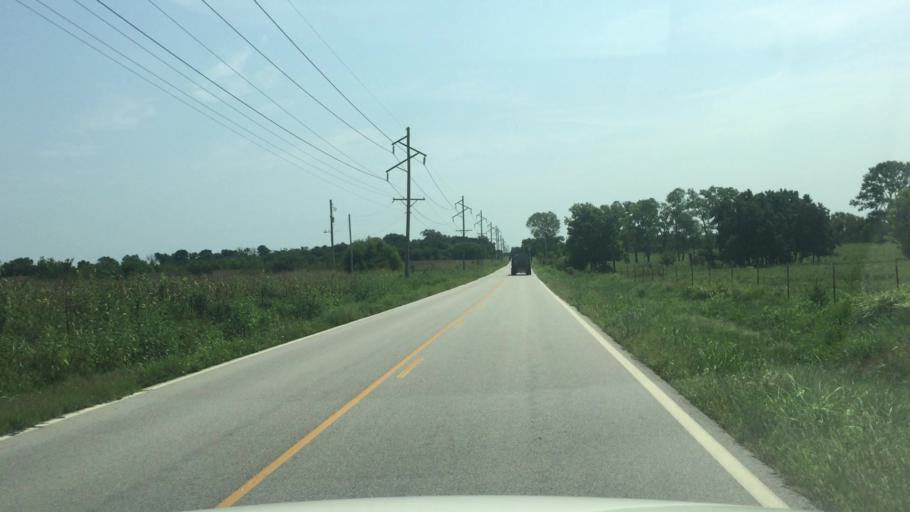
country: US
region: Kansas
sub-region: Montgomery County
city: Cherryvale
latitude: 37.2084
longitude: -95.5706
